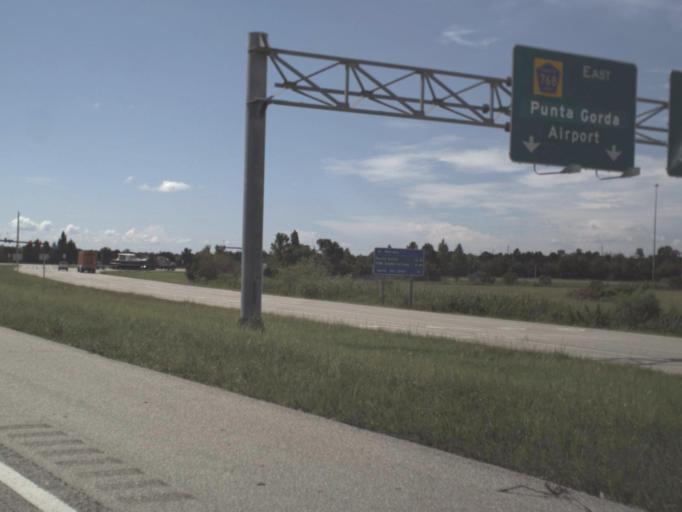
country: US
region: Florida
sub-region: Charlotte County
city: Charlotte Park
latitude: 26.8974
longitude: -82.0050
